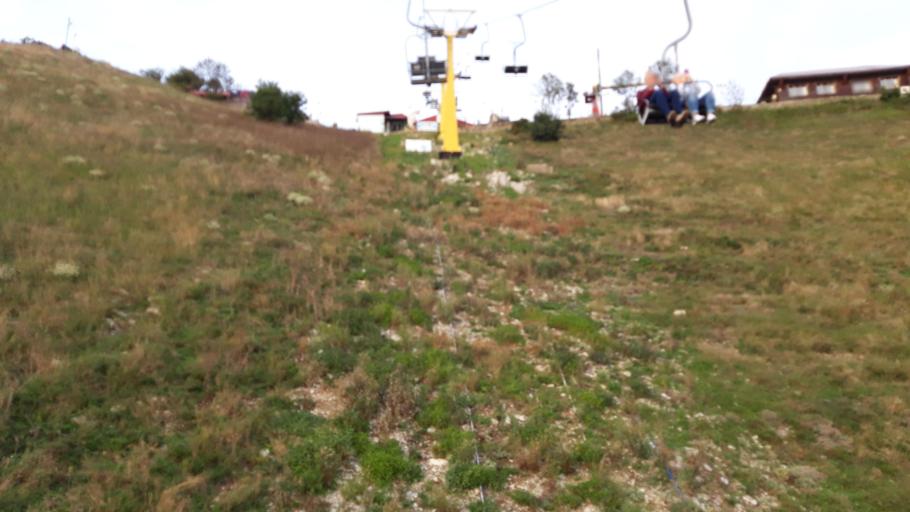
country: RU
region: Krasnodarskiy
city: Gelendzhik
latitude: 44.5845
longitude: 38.1008
